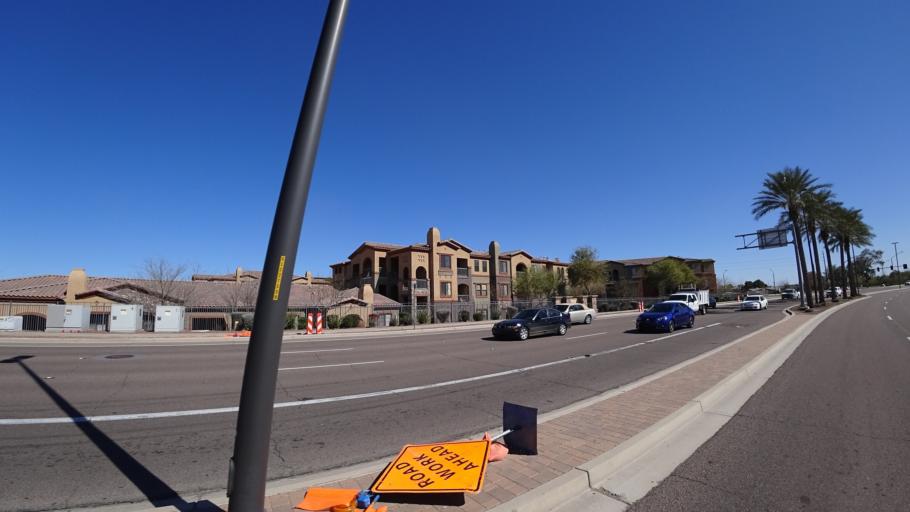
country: US
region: Arizona
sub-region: Maricopa County
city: Gilbert
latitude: 33.2963
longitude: -111.7405
